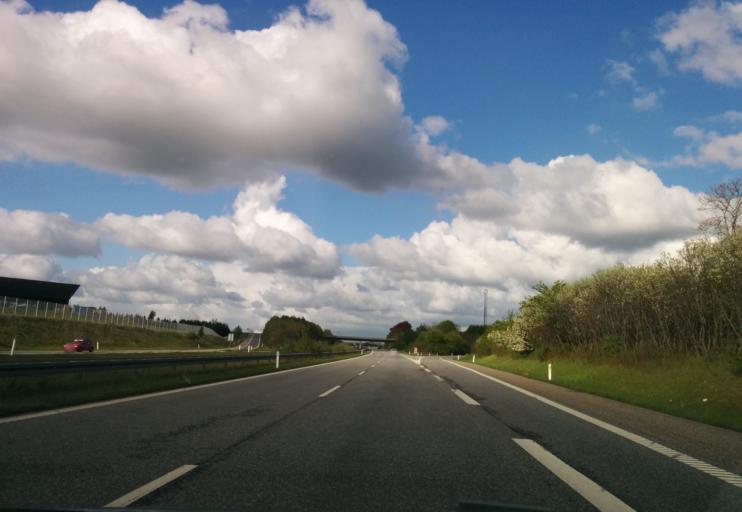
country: DK
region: Central Jutland
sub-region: Skanderborg Kommune
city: Horning
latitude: 56.1054
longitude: 10.0475
